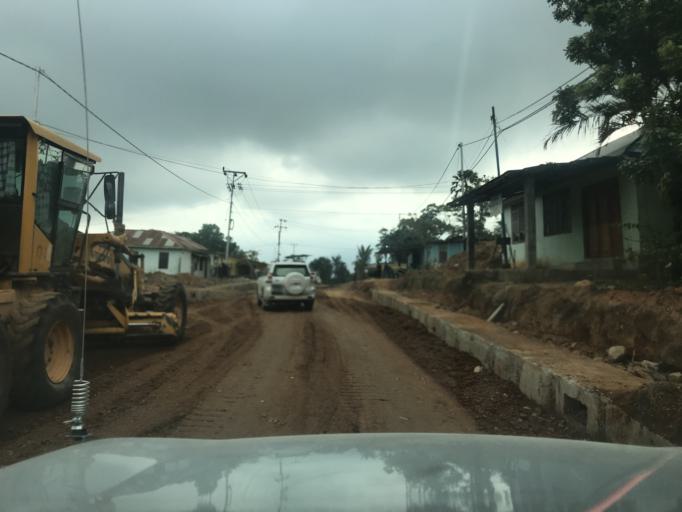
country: TL
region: Ainaro
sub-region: Ainaro
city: Ainaro
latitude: -8.9963
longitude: 125.5059
